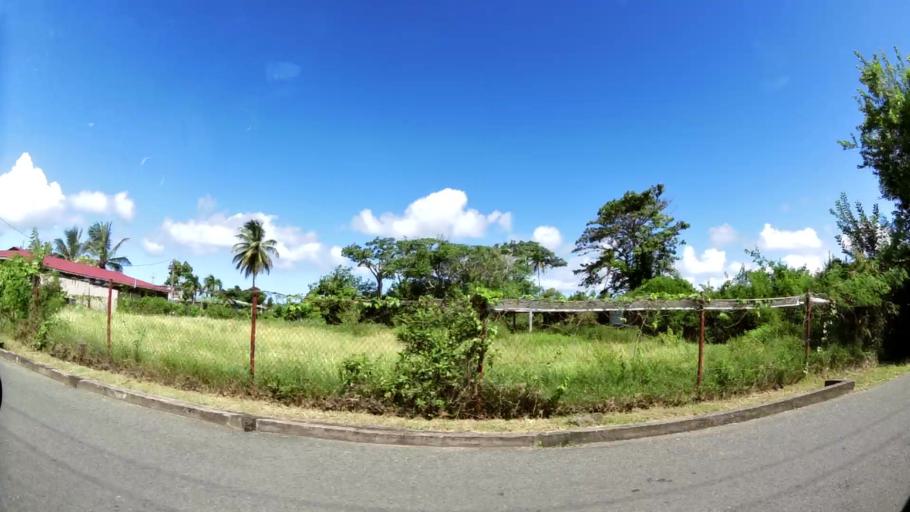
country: TT
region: Tobago
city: Scarborough
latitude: 11.1566
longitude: -60.7753
